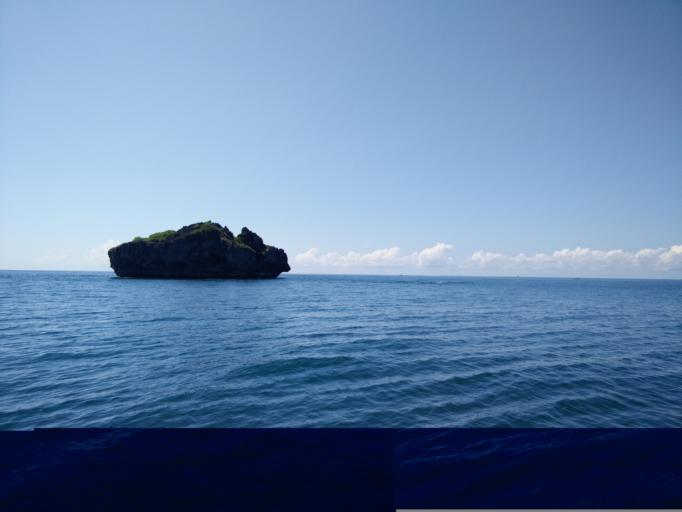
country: MM
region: Ayeyarwady
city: Pathein
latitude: 16.8547
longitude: 94.2718
